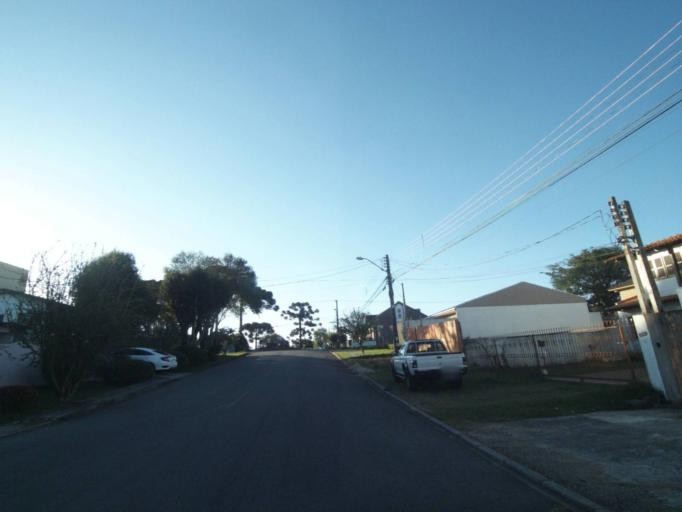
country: BR
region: Parana
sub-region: Curitiba
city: Curitiba
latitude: -25.3901
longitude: -49.2554
